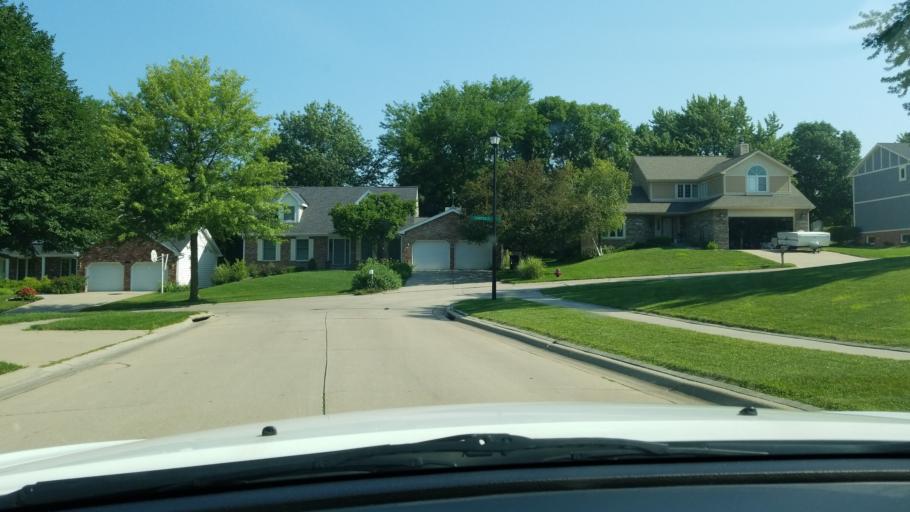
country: US
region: Nebraska
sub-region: Lancaster County
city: Lincoln
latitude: 40.8023
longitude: -96.6309
